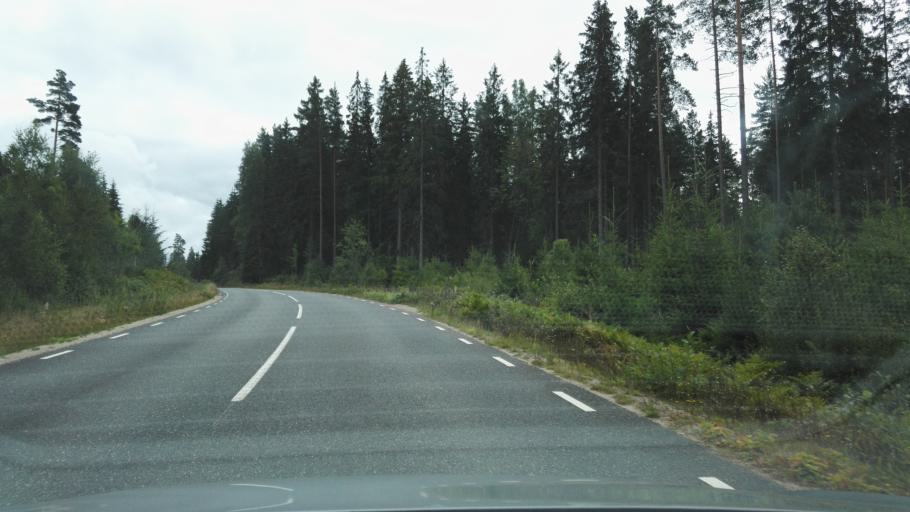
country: SE
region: Joenkoeping
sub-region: Vetlanda Kommun
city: Landsbro
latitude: 57.2574
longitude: 14.9351
